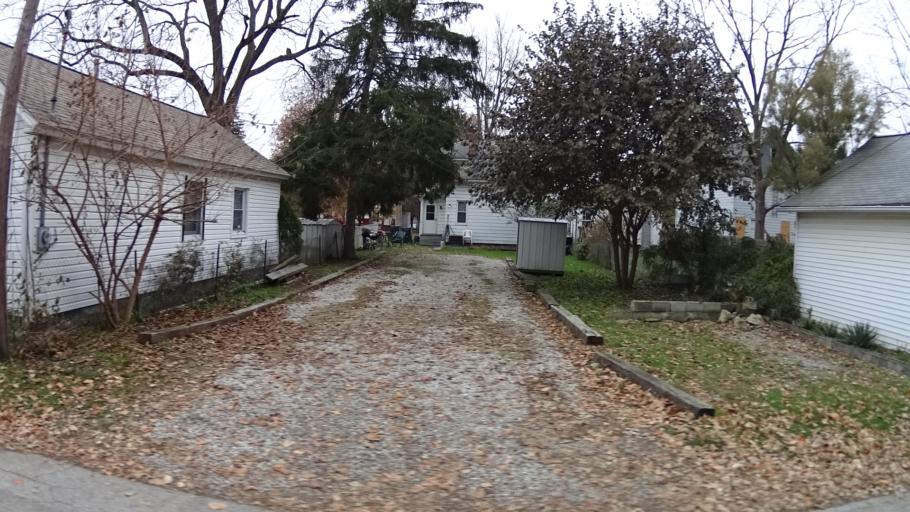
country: US
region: Ohio
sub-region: Lorain County
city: Elyria
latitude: 41.3592
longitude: -82.1082
